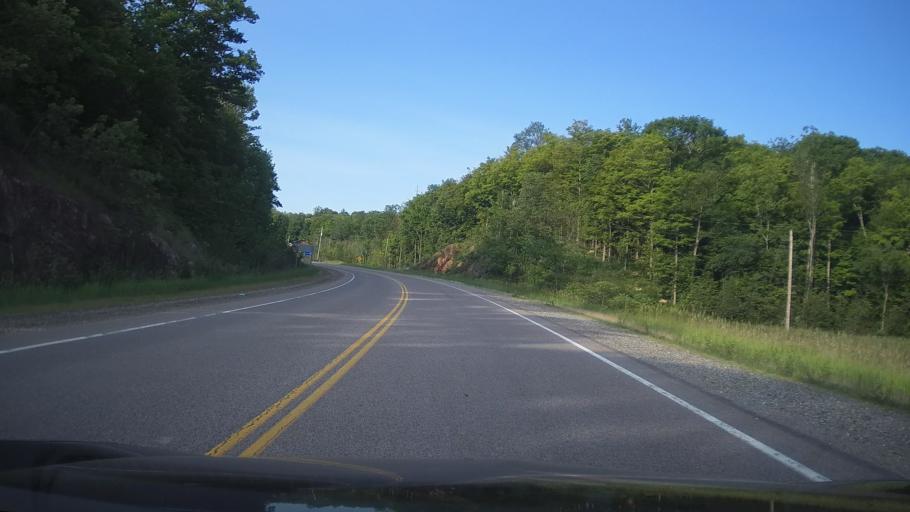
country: CA
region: Ontario
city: Perth
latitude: 44.7822
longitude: -76.7228
